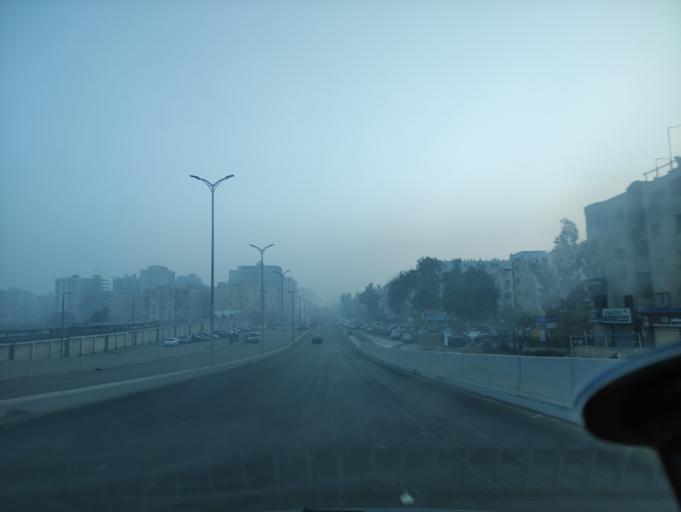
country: EG
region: Muhafazat al Qahirah
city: Cairo
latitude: 30.0467
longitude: 31.3578
